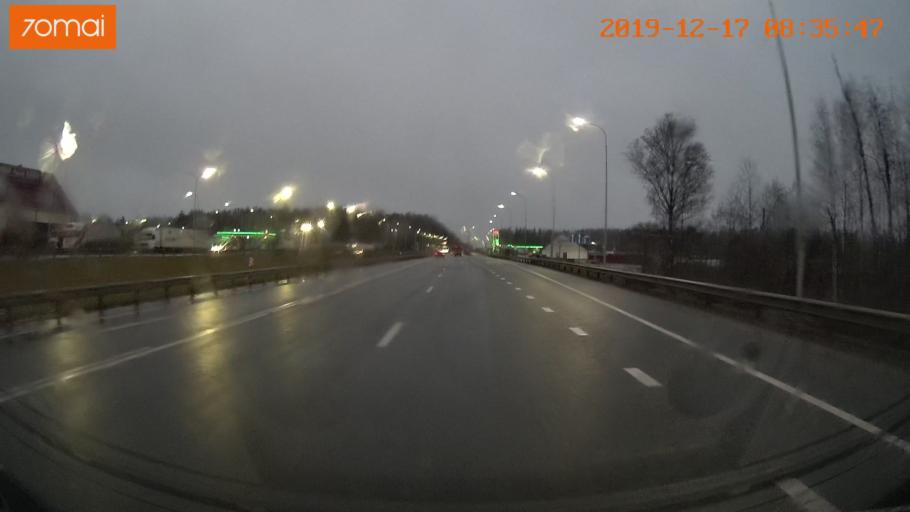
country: RU
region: Vladimir
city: Lakinsk
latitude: 55.9971
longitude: 39.8958
